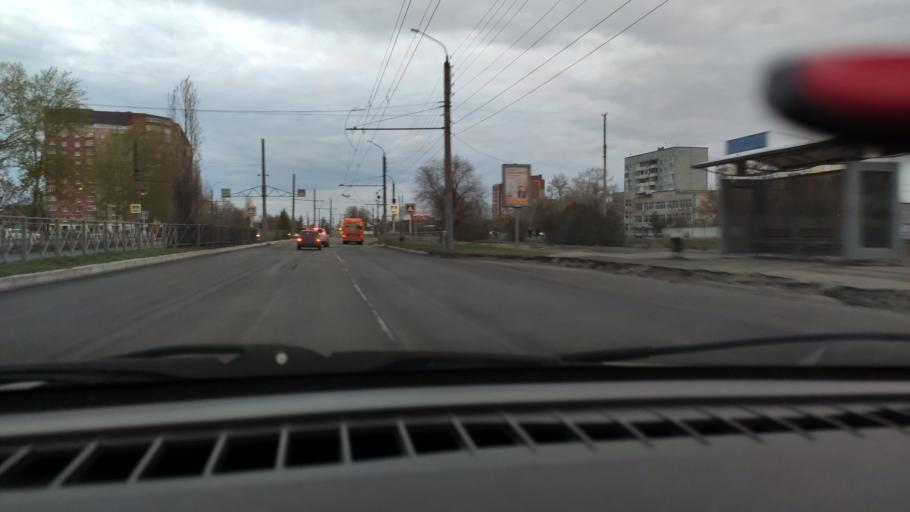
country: RU
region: Orenburg
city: Orenburg
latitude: 51.8154
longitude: 55.1076
